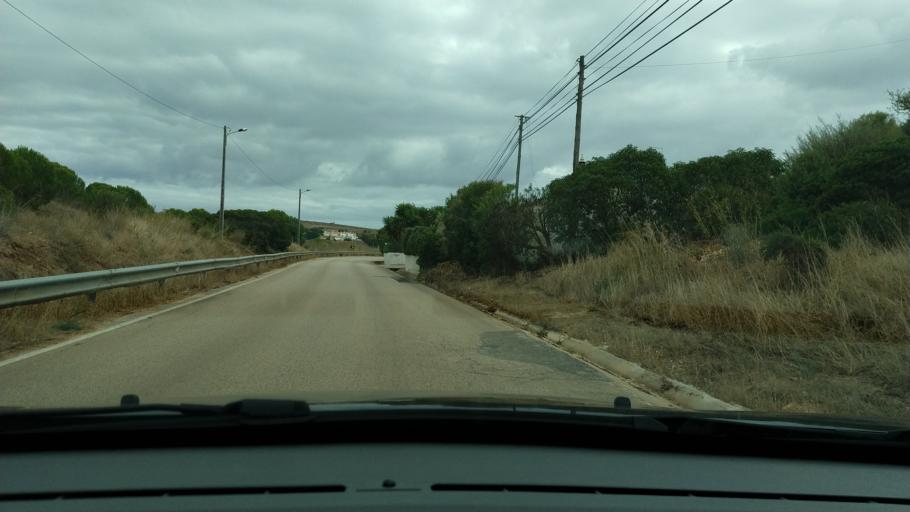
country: PT
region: Faro
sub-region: Lagos
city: Lagos
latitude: 37.0806
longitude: -8.7770
